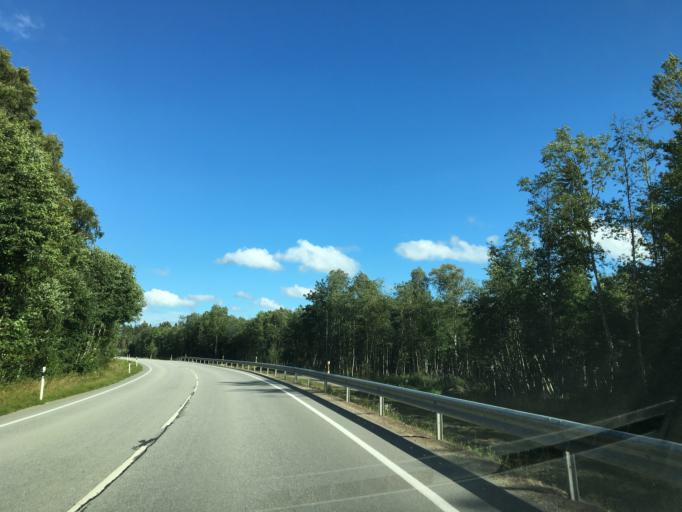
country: EE
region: Paernumaa
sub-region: Vaendra vald (alev)
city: Vandra
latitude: 58.6431
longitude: 25.0795
